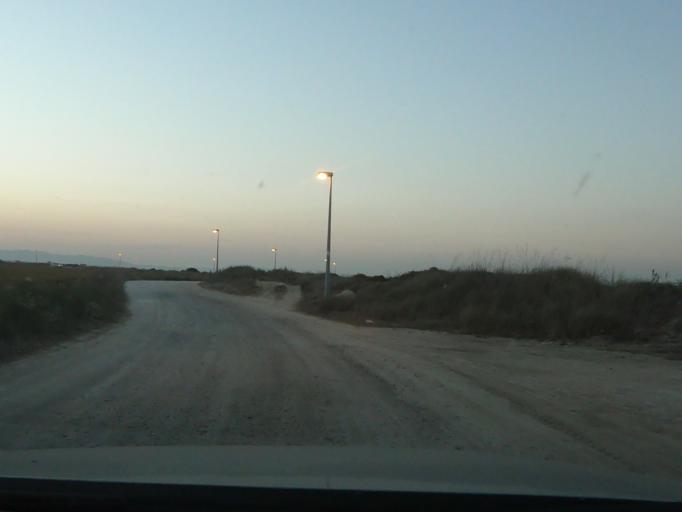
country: PT
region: Setubal
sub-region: Setubal
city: Setubal
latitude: 38.4124
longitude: -8.7532
